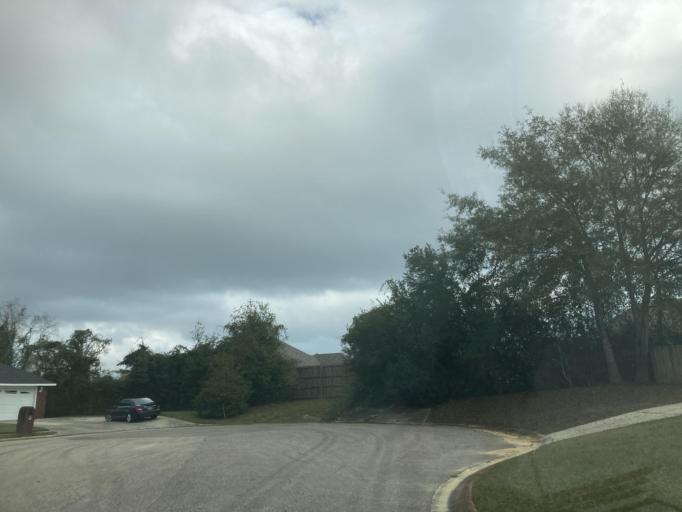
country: US
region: Mississippi
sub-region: Jackson County
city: Latimer
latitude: 30.5063
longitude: -88.9685
